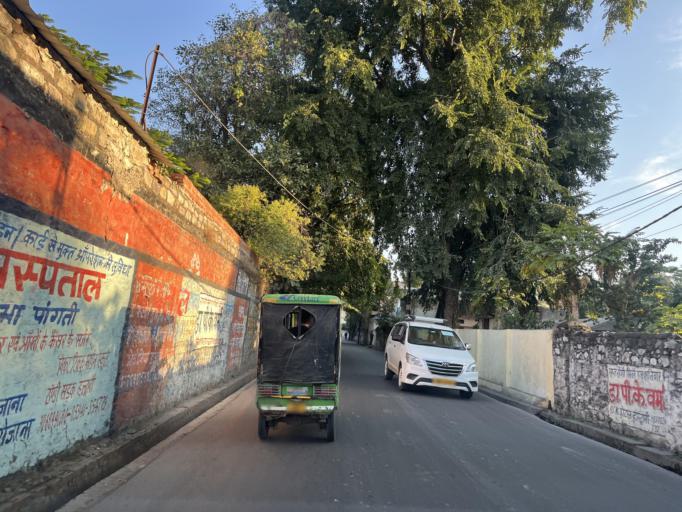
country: IN
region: Uttarakhand
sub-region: Naini Tal
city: Haldwani
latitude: 29.2158
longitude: 79.5258
